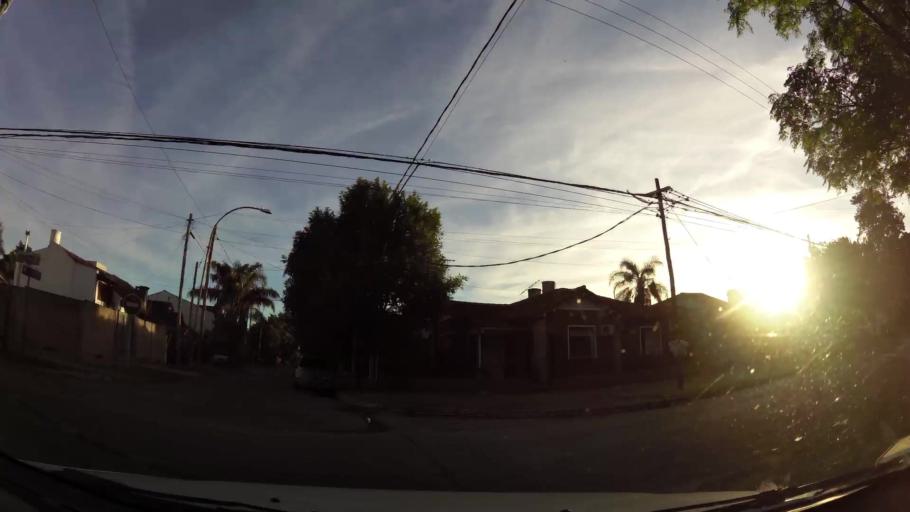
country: AR
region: Buenos Aires
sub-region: Partido de Moron
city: Moron
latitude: -34.6433
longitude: -58.6382
